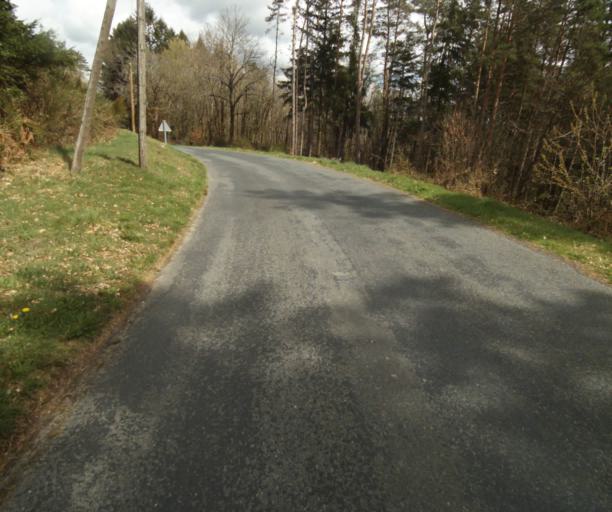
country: FR
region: Limousin
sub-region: Departement de la Correze
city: Correze
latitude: 45.3726
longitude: 1.9351
